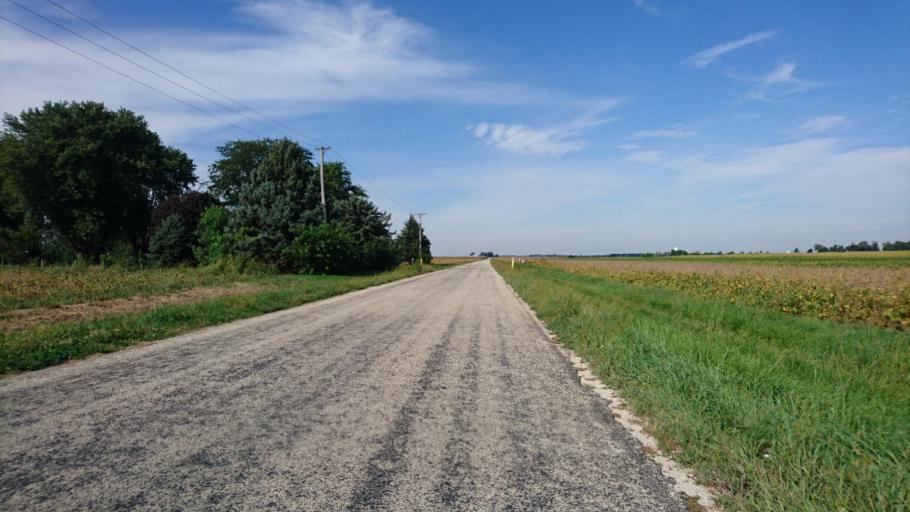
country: US
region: Illinois
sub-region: Will County
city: Manhattan
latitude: 41.4166
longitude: -88.0284
